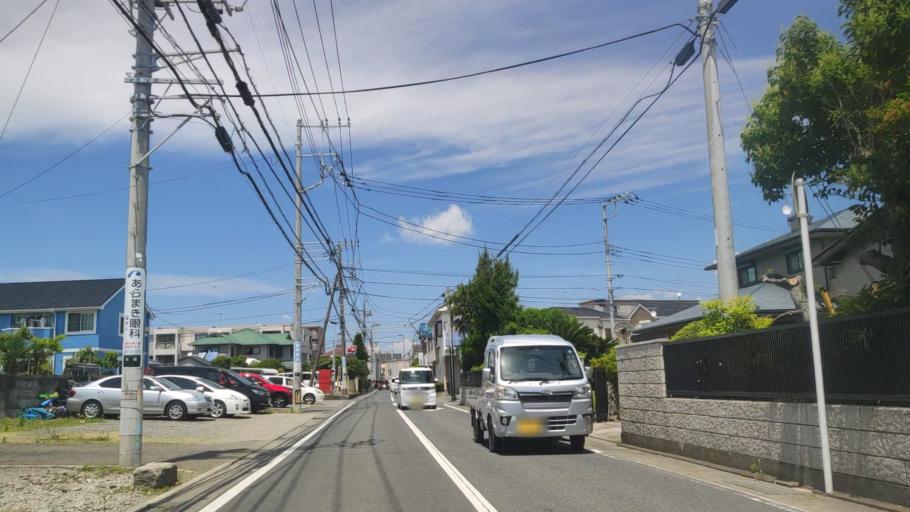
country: JP
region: Kanagawa
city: Chigasaki
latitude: 35.3411
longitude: 139.3976
